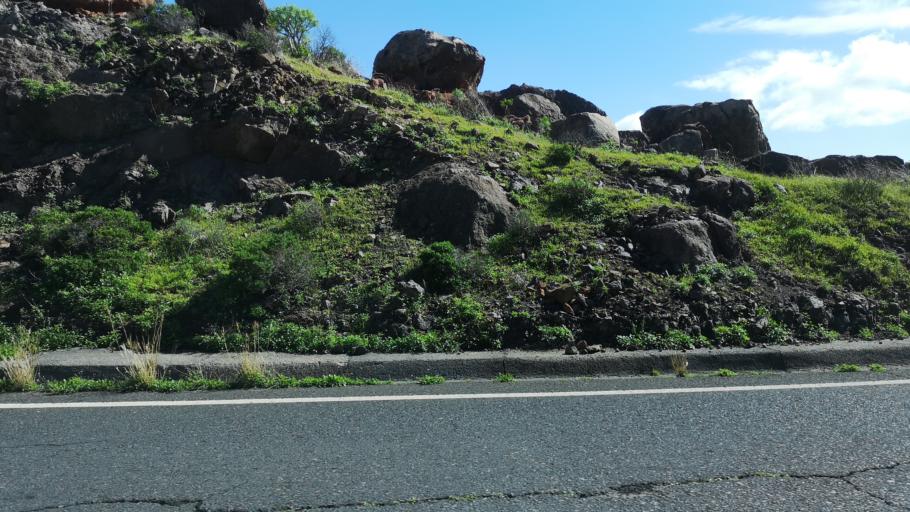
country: ES
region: Canary Islands
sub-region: Provincia de Santa Cruz de Tenerife
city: Alajero
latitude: 28.0809
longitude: -17.2017
